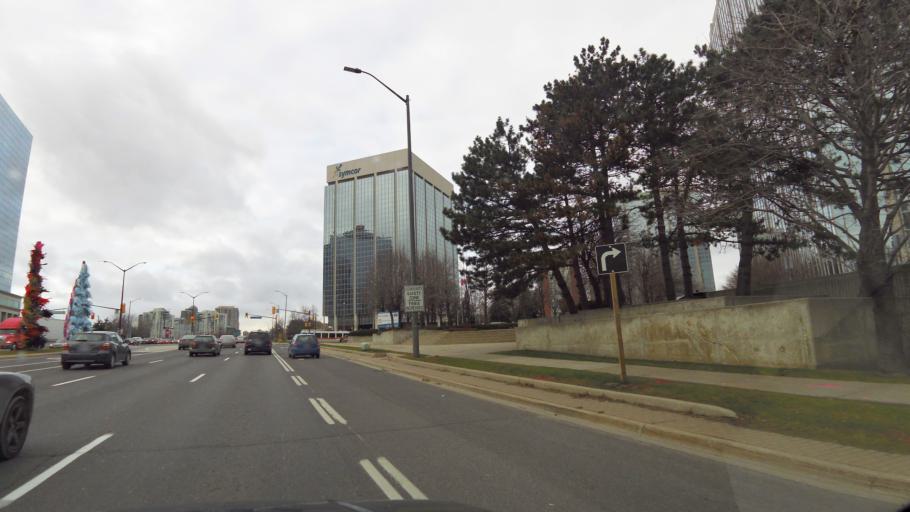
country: CA
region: Ontario
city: Mississauga
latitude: 43.5956
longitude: -79.6374
